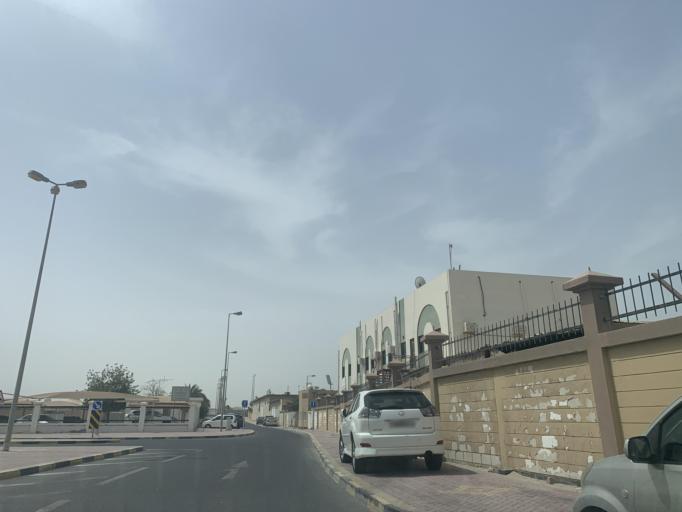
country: BH
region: Northern
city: Madinat `Isa
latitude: 26.1595
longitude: 50.5475
